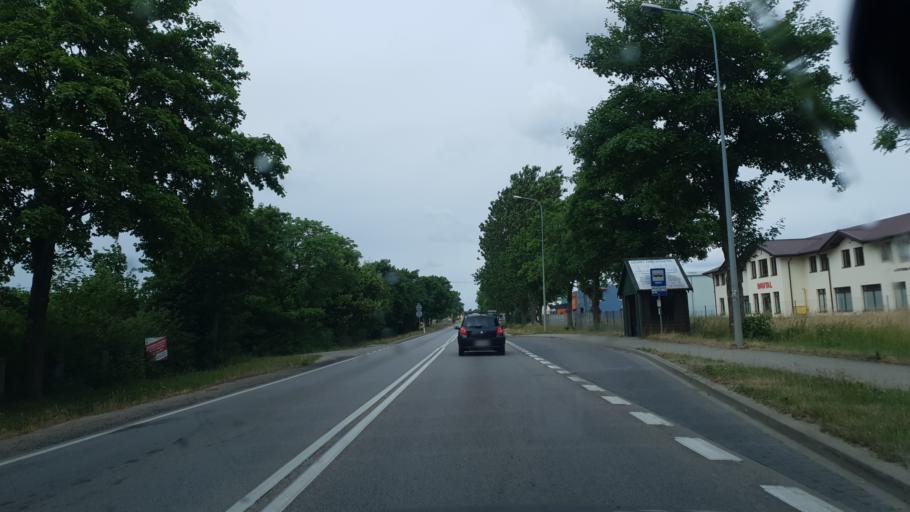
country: PL
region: Pomeranian Voivodeship
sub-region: Powiat kartuski
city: Banino
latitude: 54.4108
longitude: 18.3709
